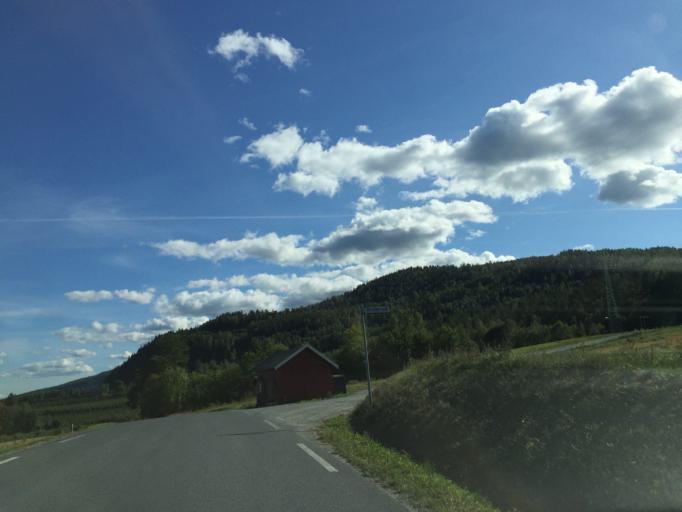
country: NO
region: Buskerud
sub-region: Ovre Eiker
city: Hokksund
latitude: 59.6895
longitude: 9.8474
